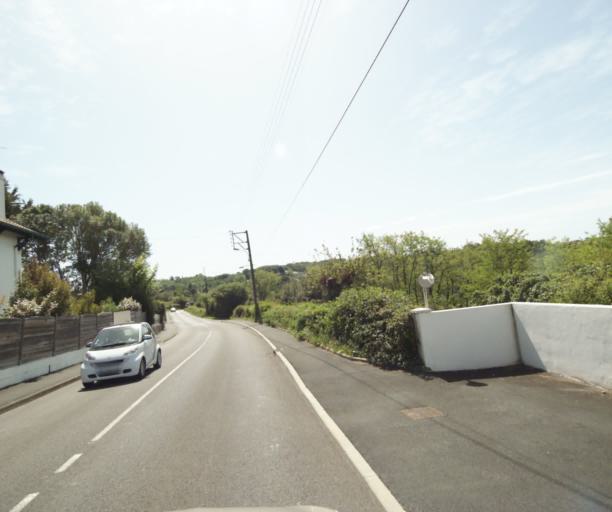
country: FR
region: Aquitaine
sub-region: Departement des Pyrenees-Atlantiques
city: Mouguerre
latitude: 43.4660
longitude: -1.4441
